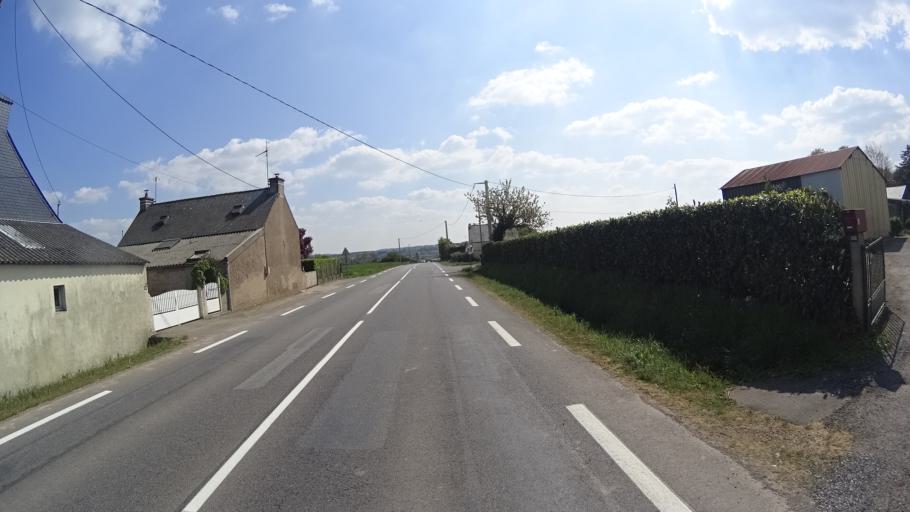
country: FR
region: Brittany
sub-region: Departement du Morbihan
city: Rieux
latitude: 47.5893
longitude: -2.1102
